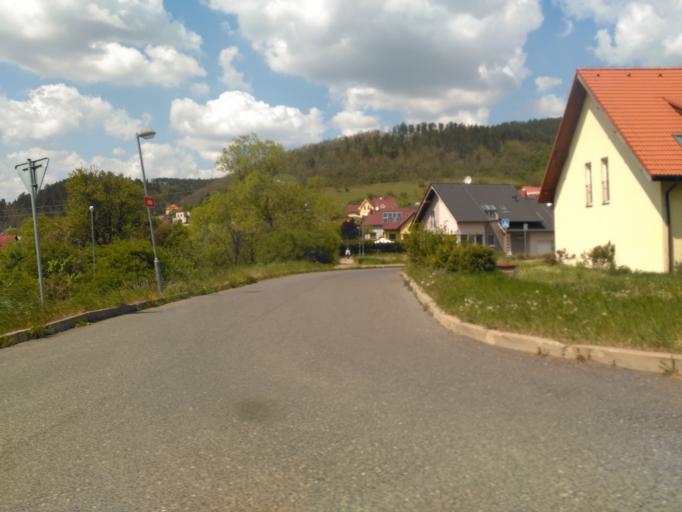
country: CZ
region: Central Bohemia
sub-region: Okres Beroun
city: Kraluv Dvur
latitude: 49.9524
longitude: 14.0305
